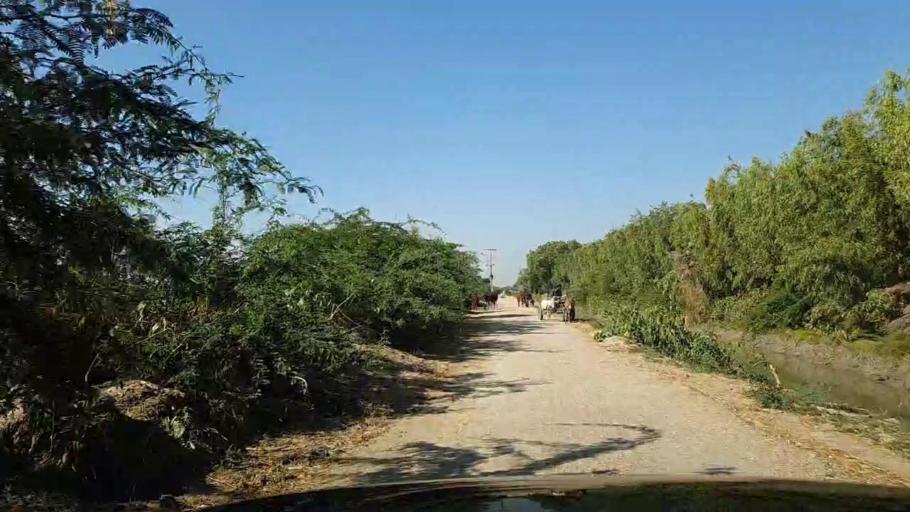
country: PK
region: Sindh
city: Thatta
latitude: 24.7086
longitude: 67.9163
